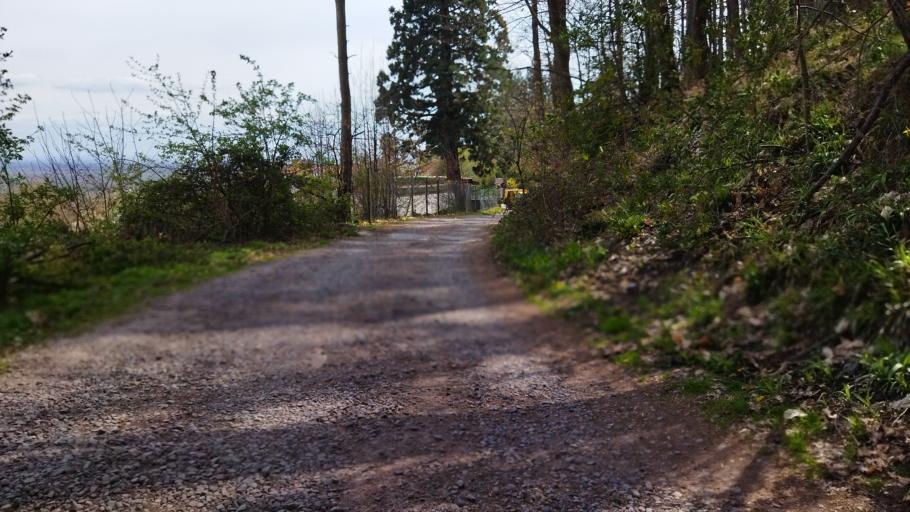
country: DE
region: Rheinland-Pfalz
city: Burrweiler
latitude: 49.2731
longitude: 8.0809
